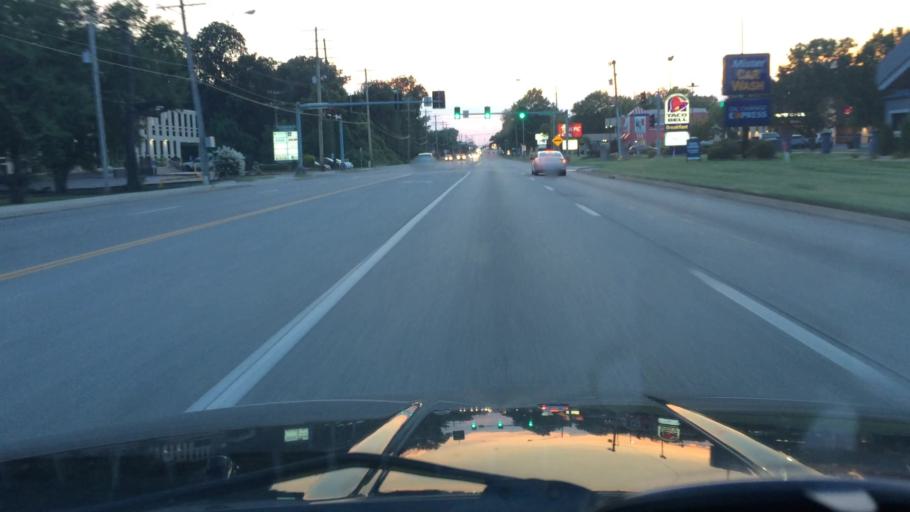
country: US
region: Missouri
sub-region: Greene County
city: Springfield
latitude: 37.1812
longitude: -93.2504
